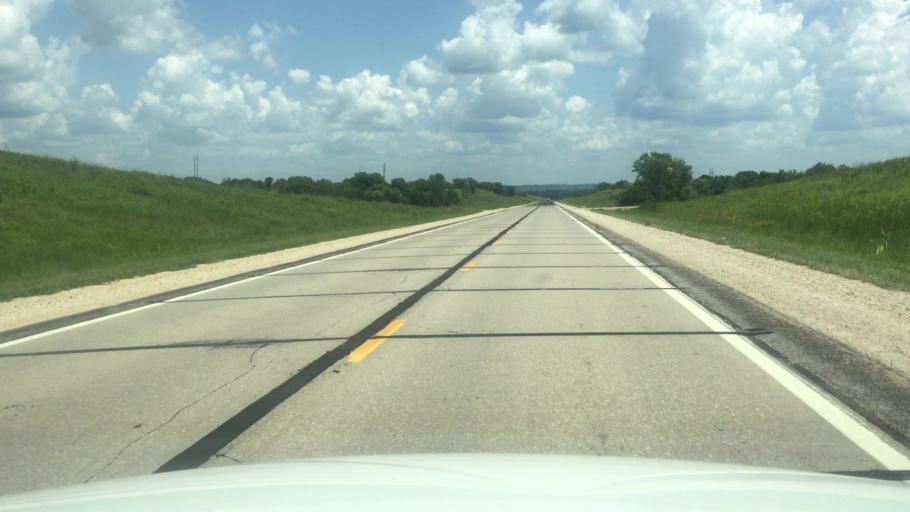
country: US
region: Kansas
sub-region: Atchison County
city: Atchison
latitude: 39.5571
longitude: -95.1832
